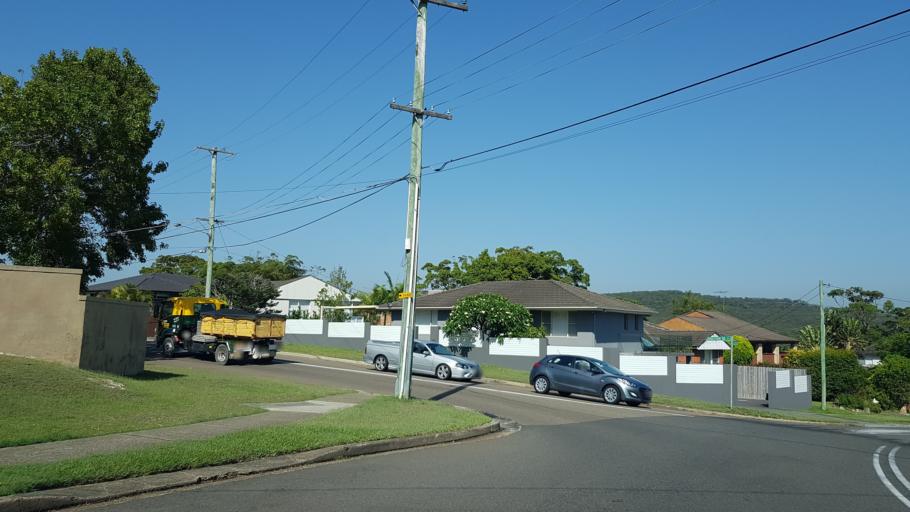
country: AU
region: New South Wales
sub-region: Warringah
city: Narrabeen
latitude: -33.7268
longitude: 151.2806
